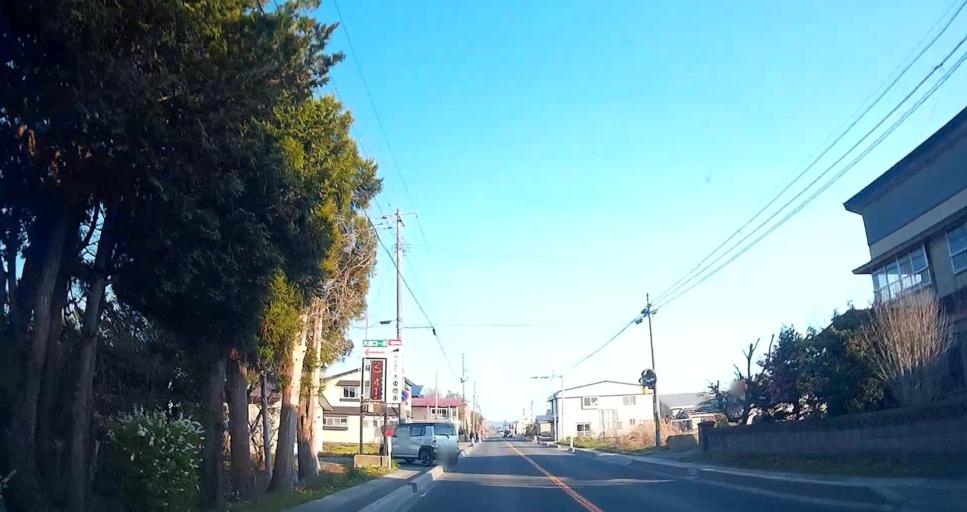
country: JP
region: Aomori
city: Mutsu
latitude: 41.2700
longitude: 141.2188
